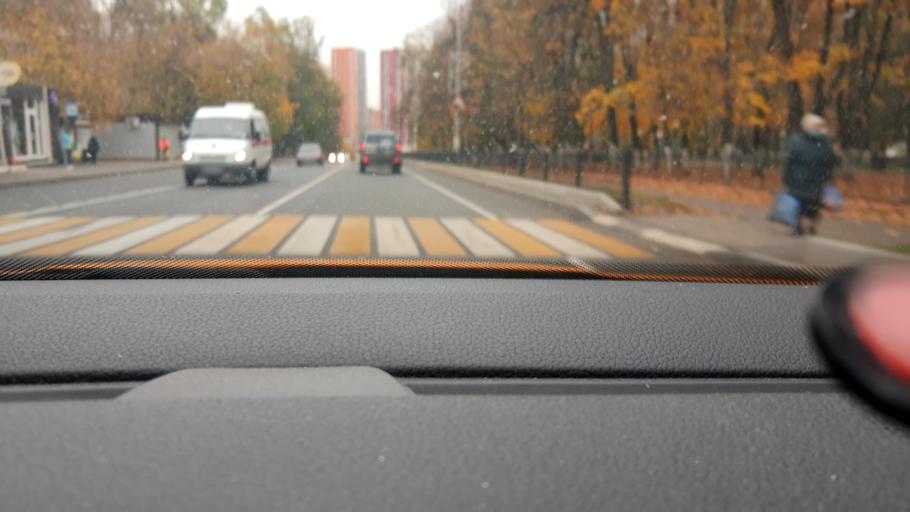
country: RU
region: Moskovskaya
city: Krasnogorsk
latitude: 55.8222
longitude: 37.3383
